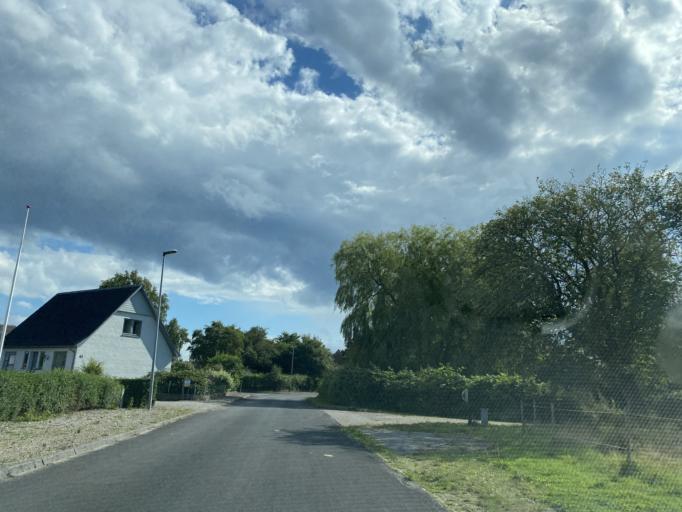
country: DK
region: South Denmark
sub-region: Haderslev Kommune
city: Starup
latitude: 55.2066
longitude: 9.5164
